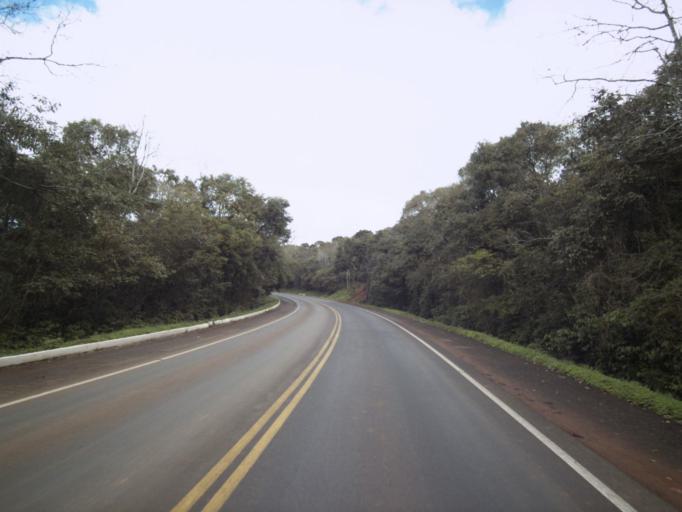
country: BR
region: Santa Catarina
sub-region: Concordia
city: Concordia
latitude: -27.3528
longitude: -51.9893
